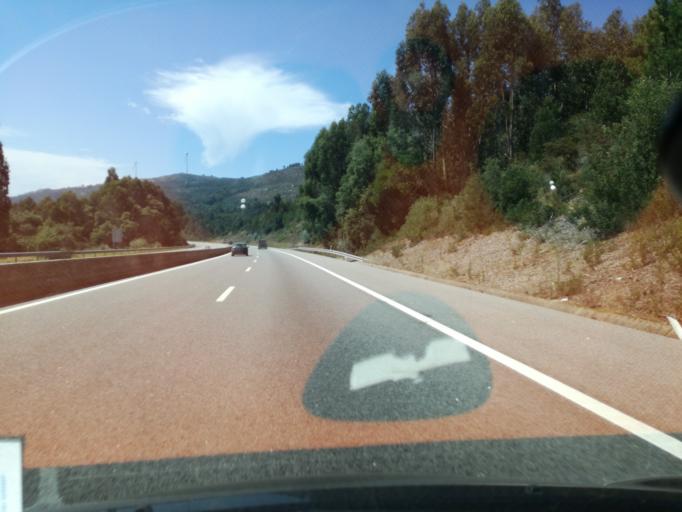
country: PT
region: Viana do Castelo
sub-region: Viana do Castelo
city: Meadela
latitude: 41.7696
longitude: -8.7862
